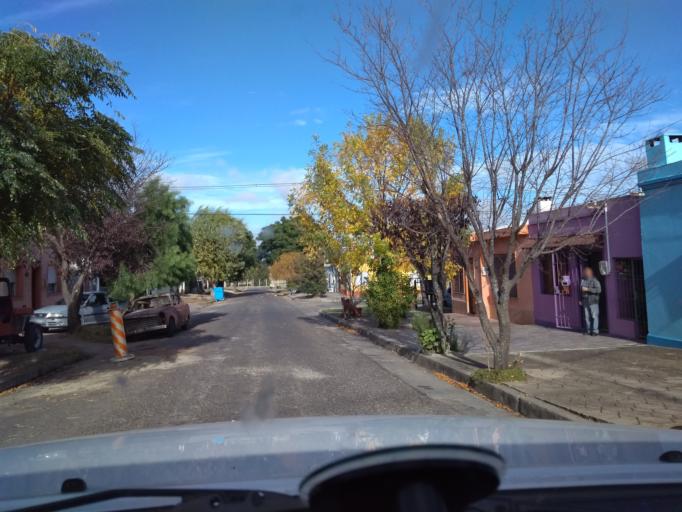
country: UY
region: Florida
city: Florida
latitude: -34.1063
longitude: -56.2143
